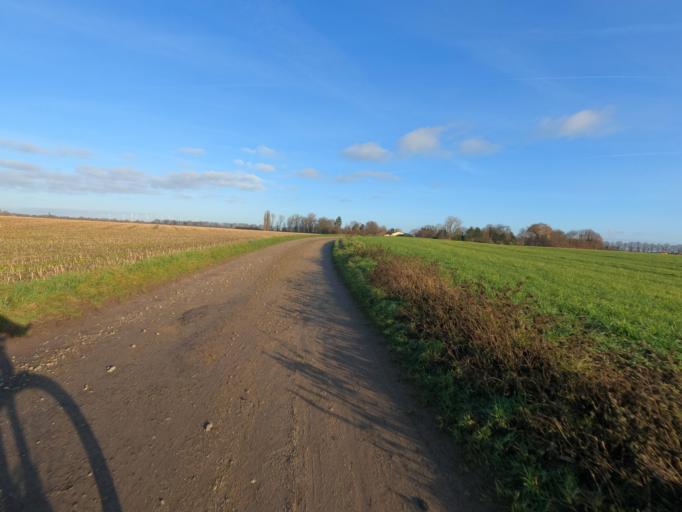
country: DE
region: North Rhine-Westphalia
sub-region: Regierungsbezirk Koln
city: Bedburg
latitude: 50.9832
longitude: 6.5005
